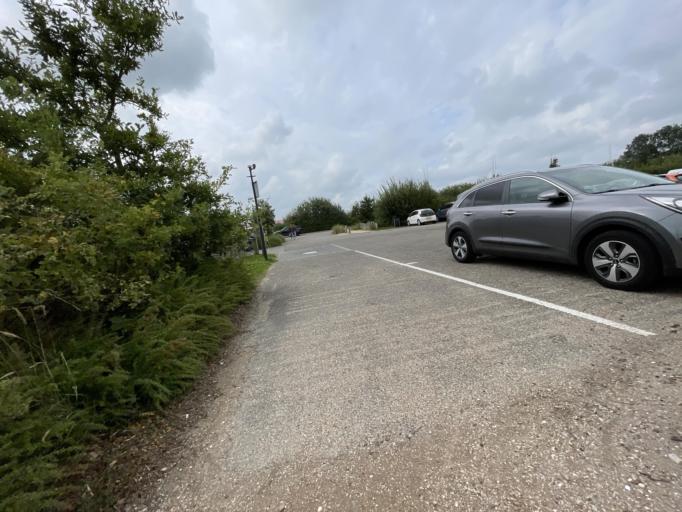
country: NL
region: Zeeland
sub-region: Schouwen-Duiveland
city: Renesse
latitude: 51.7378
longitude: 3.8024
